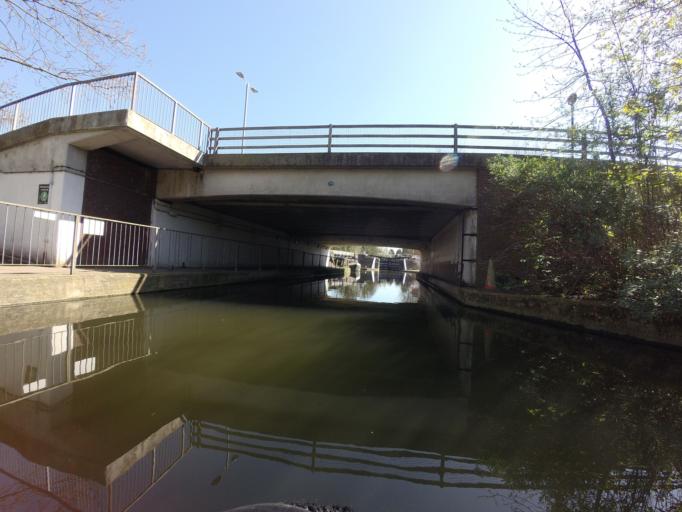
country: GB
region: England
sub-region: Hertfordshire
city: Rickmansworth
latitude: 51.6348
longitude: -0.4675
